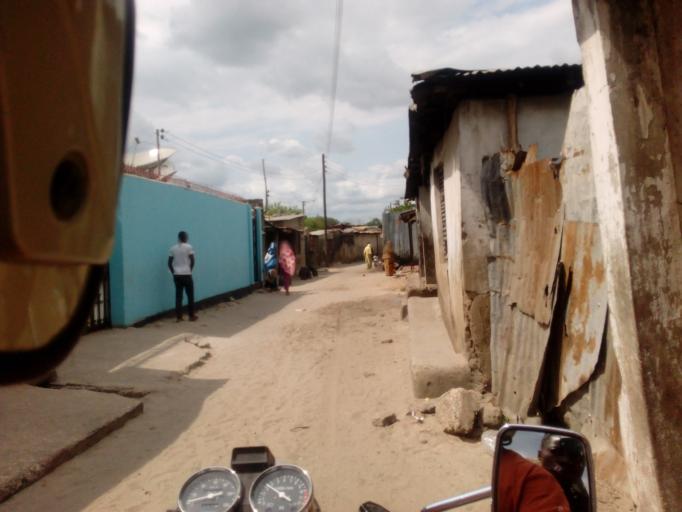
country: TZ
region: Dar es Salaam
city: Dar es Salaam
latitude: -6.8543
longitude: 39.2562
